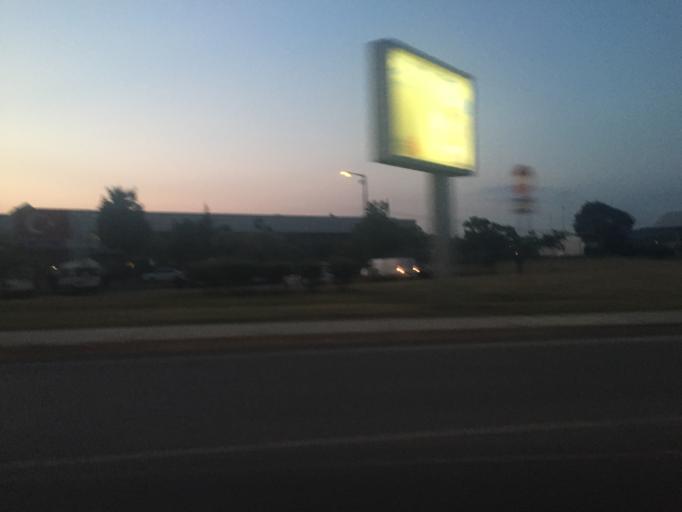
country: TR
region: Istanbul
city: Pendik
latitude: 40.9110
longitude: 29.3158
